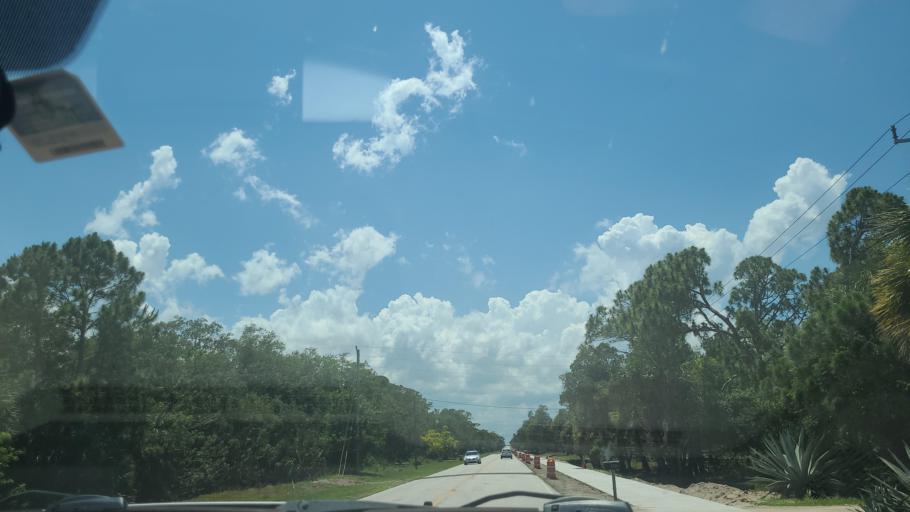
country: US
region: Florida
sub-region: Brevard County
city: Grant-Valkaria
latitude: 27.9537
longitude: -80.5954
